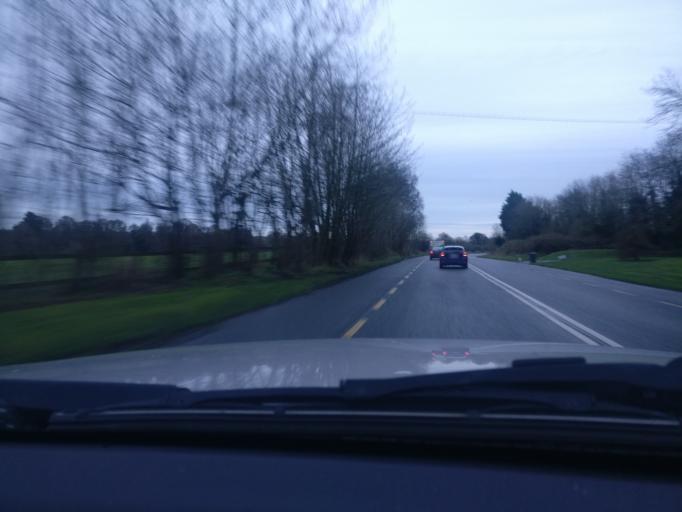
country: IE
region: Leinster
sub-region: An Mhi
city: Kells
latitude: 53.7101
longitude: -6.8080
